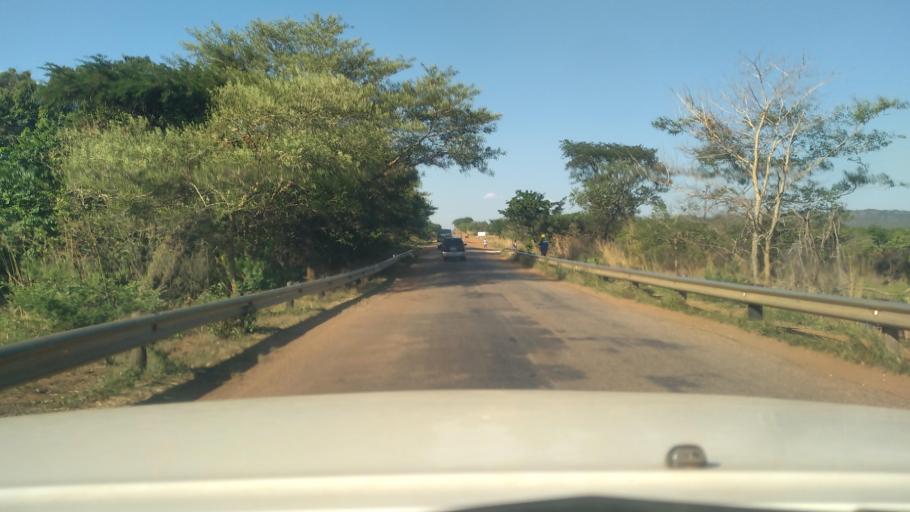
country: ZM
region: Northern
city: Mpika
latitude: -11.7423
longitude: 31.4685
